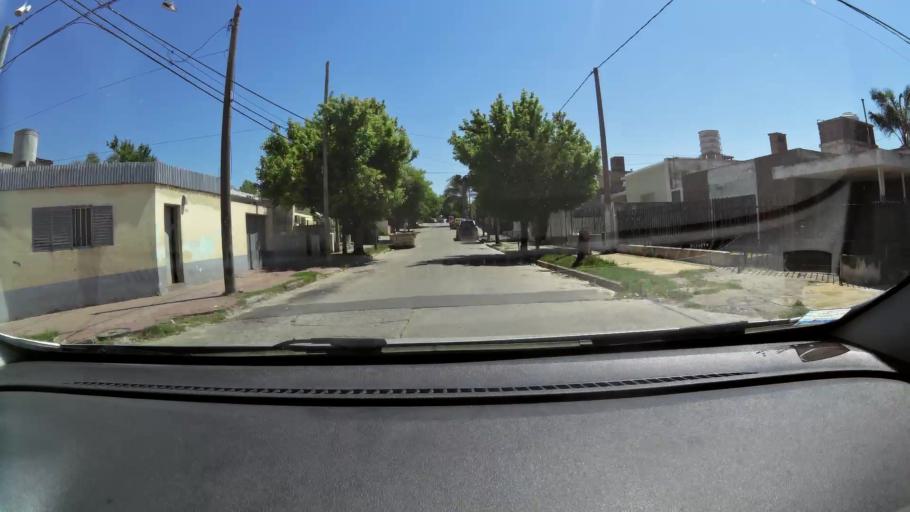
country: AR
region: Cordoba
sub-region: Departamento de Capital
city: Cordoba
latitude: -31.4336
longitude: -64.2092
